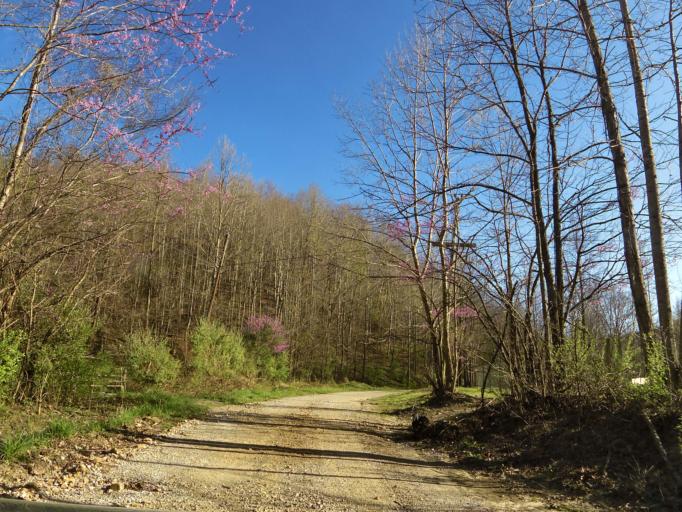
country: US
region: Tennessee
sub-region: Roane County
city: Oliver Springs
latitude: 36.2146
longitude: -84.4146
